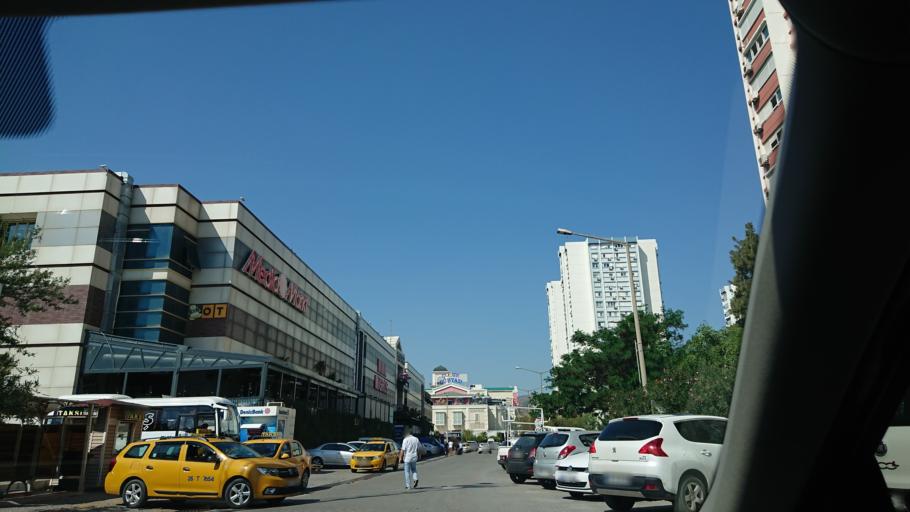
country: TR
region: Izmir
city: Karsiyaka
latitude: 38.4699
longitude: 27.0755
